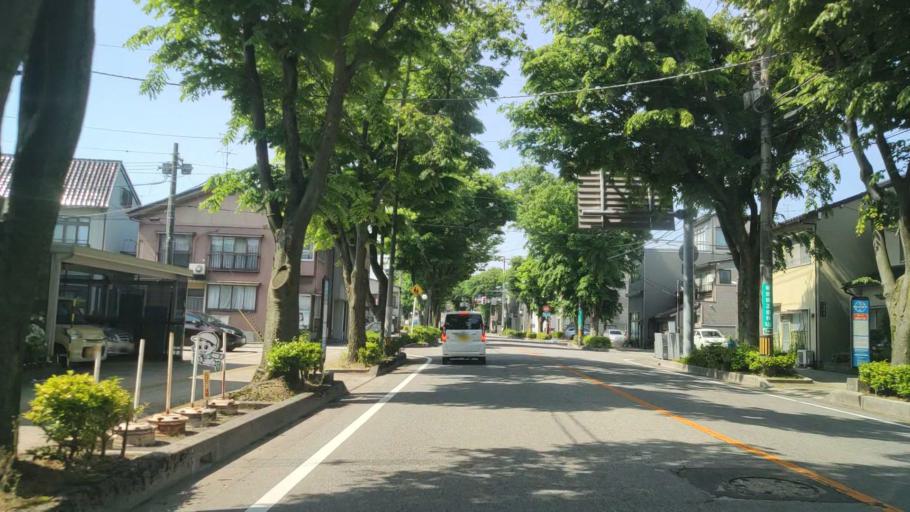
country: JP
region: Toyama
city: Toyama-shi
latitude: 36.6994
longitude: 137.2061
